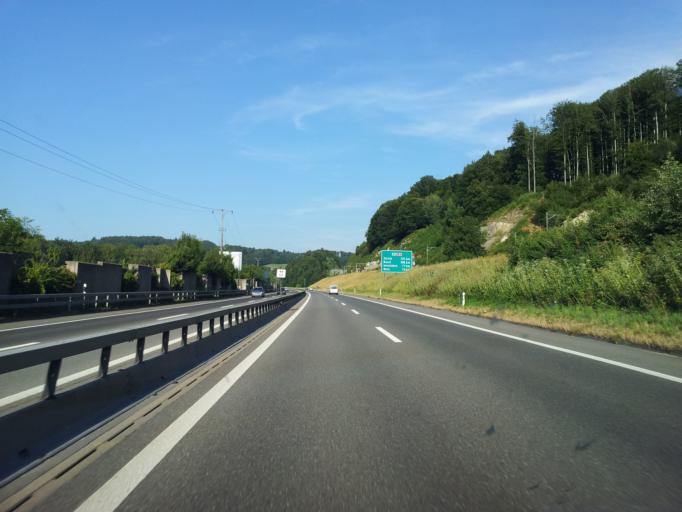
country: CH
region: Fribourg
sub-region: Sense District
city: Flamatt
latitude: 46.8883
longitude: 7.3337
